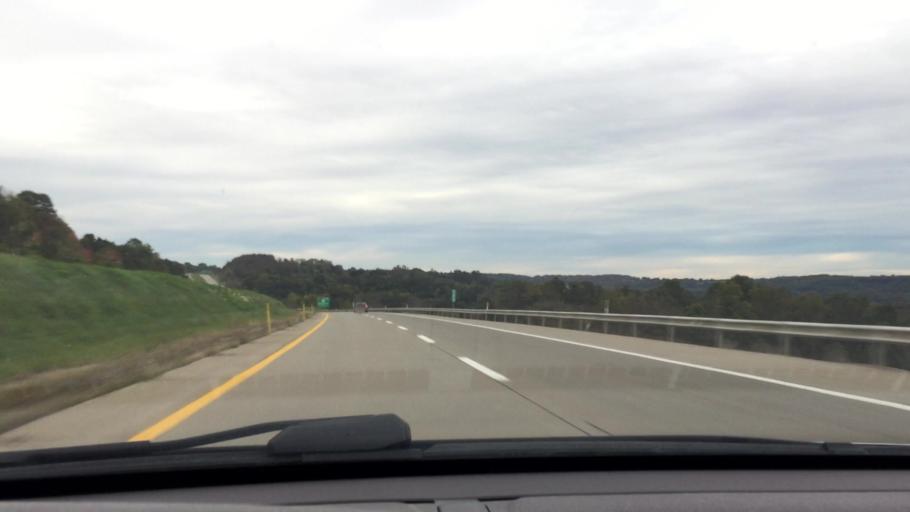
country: US
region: Pennsylvania
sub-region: Lawrence County
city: Oakland
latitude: 40.9501
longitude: -80.3920
